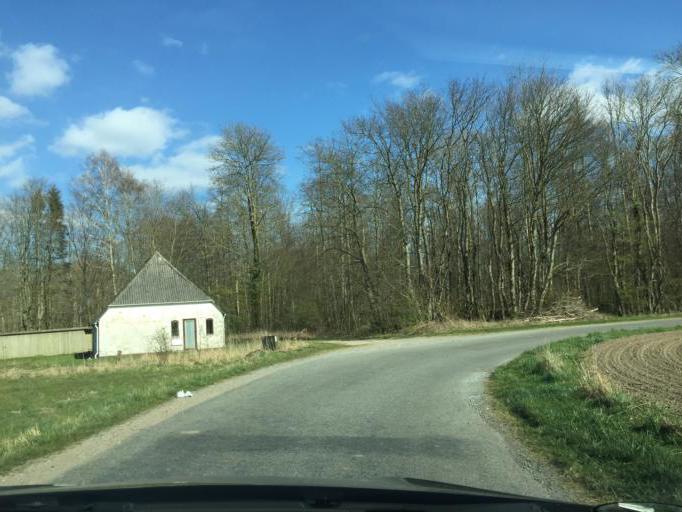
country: DK
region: South Denmark
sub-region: Faaborg-Midtfyn Kommune
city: Arslev
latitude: 55.3010
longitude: 10.4955
